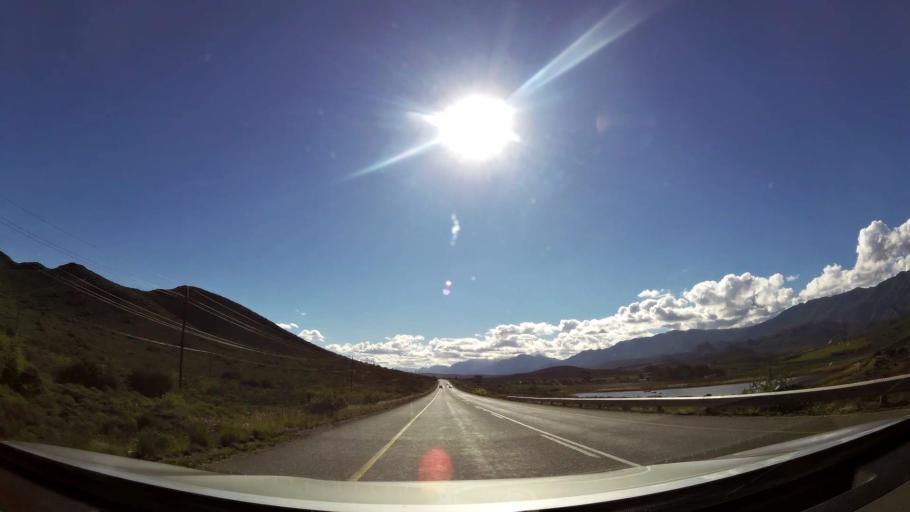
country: ZA
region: Western Cape
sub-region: Cape Winelands District Municipality
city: Ashton
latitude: -33.7835
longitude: 19.7696
